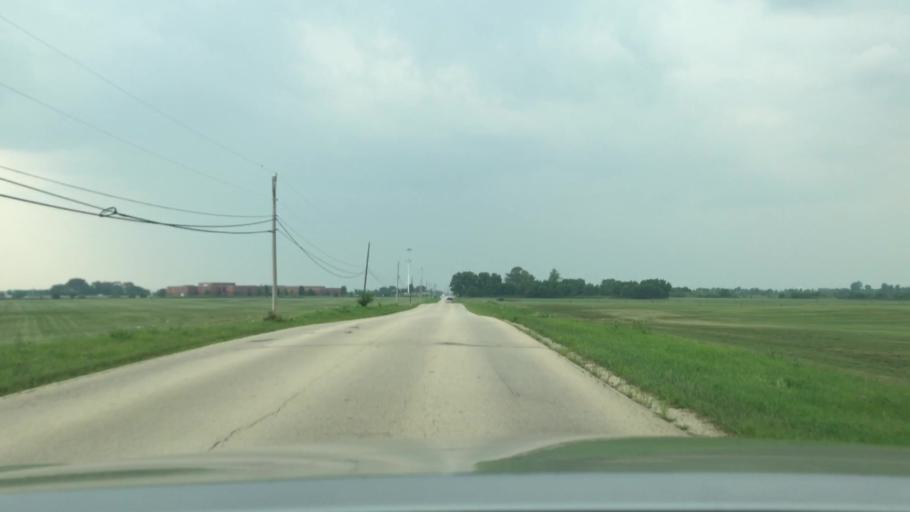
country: US
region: Illinois
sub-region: Will County
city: Plainfield
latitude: 41.6875
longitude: -88.2537
